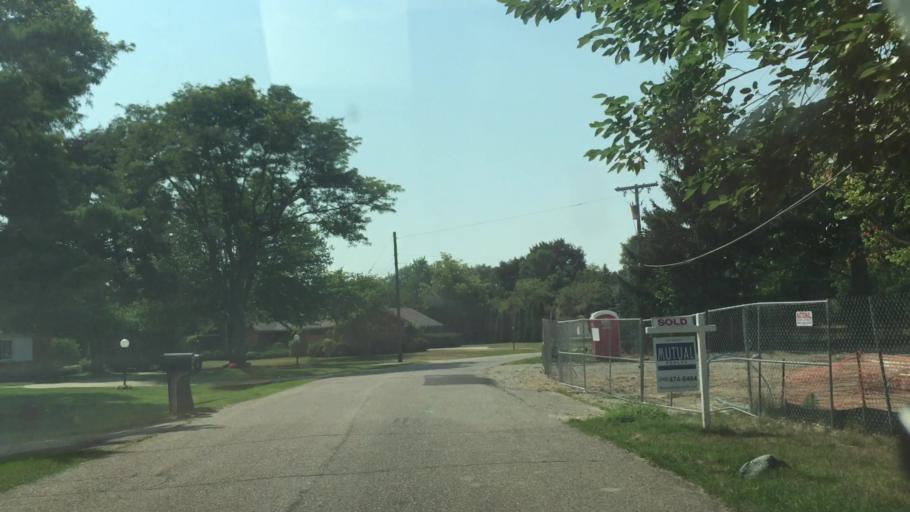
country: US
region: Michigan
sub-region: Oakland County
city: Franklin
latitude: 42.5381
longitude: -83.3150
